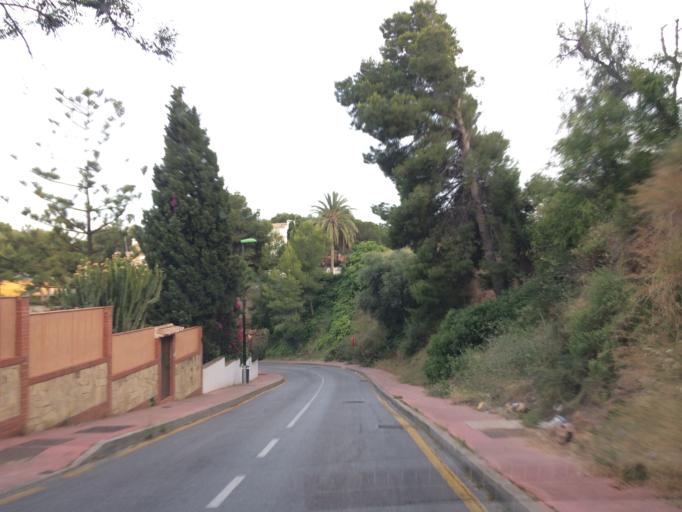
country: ES
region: Andalusia
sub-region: Provincia de Malaga
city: Malaga
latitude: 36.7264
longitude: -4.3850
